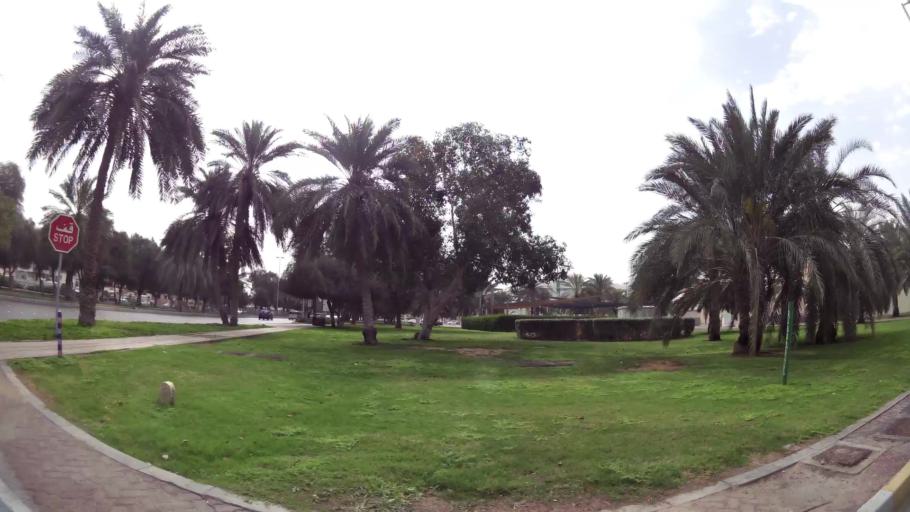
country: AE
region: Abu Dhabi
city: Abu Dhabi
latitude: 24.4566
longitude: 54.3745
